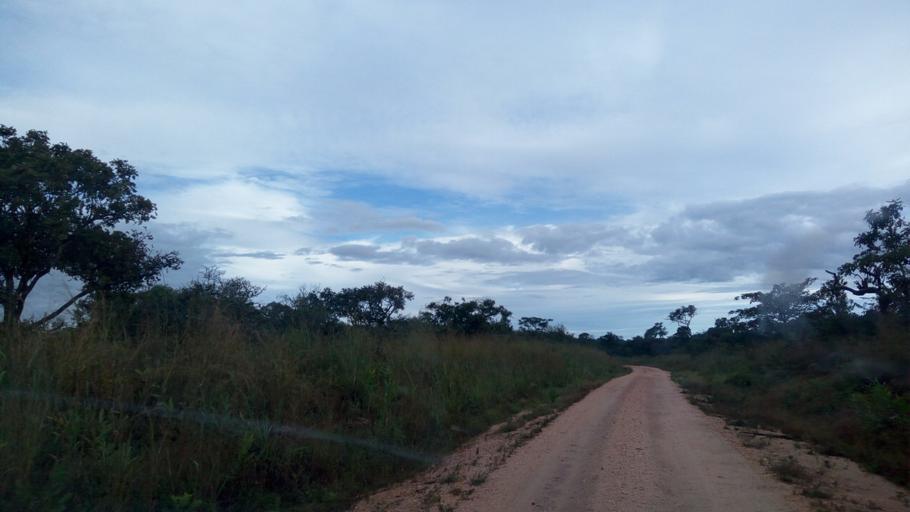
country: CD
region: Katanga
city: Kalemie
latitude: -6.5540
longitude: 29.0212
